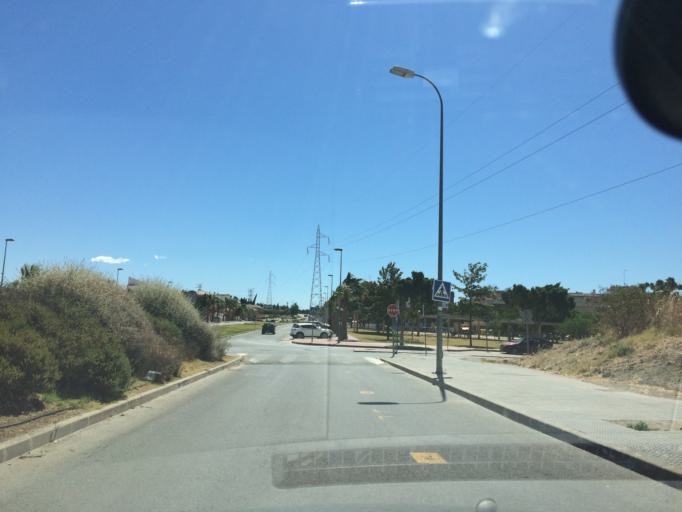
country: ES
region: Andalusia
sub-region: Provincia de Malaga
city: Estacion de Cartama
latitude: 36.7392
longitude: -4.6082
